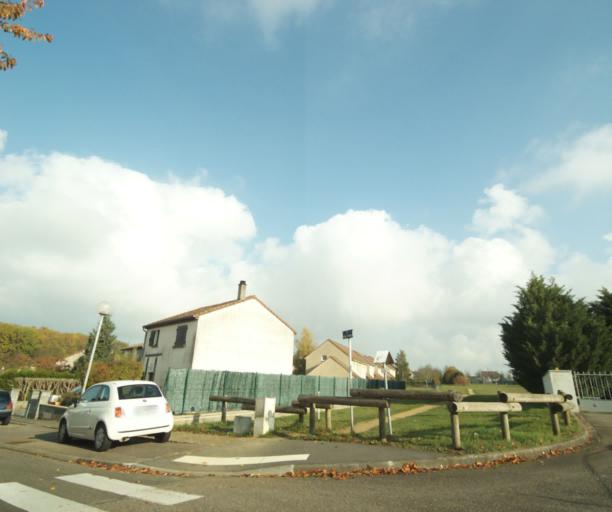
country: FR
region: Lorraine
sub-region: Departement de Meurthe-et-Moselle
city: Briey
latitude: 49.2564
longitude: 5.9368
